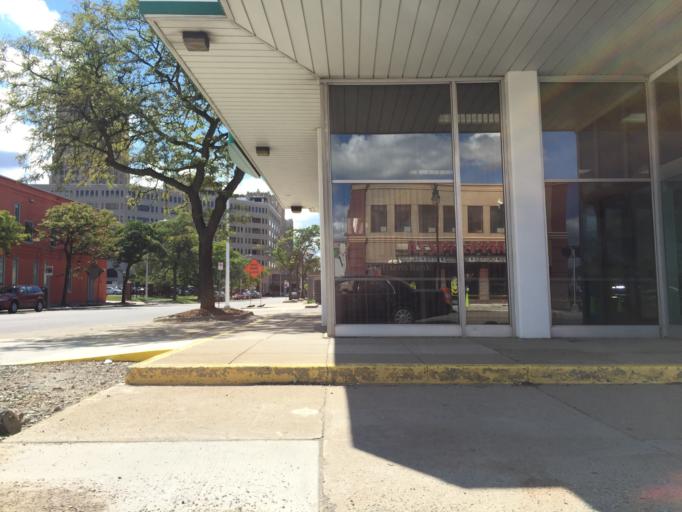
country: US
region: Michigan
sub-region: Wayne County
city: Hamtramck
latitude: 42.3717
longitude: -83.0744
